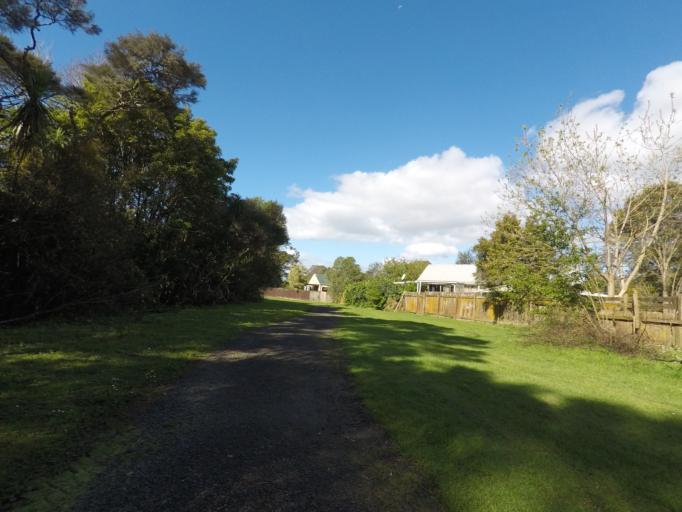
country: NZ
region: Auckland
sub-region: Auckland
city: Rosebank
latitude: -36.8602
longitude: 174.5956
